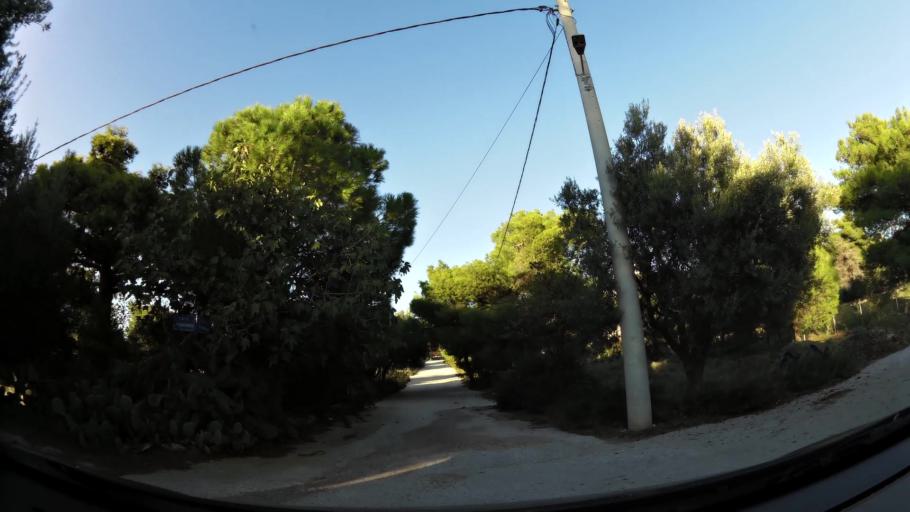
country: GR
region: Attica
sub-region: Nomarchia Athinas
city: Penteli
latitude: 38.0420
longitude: 23.8562
